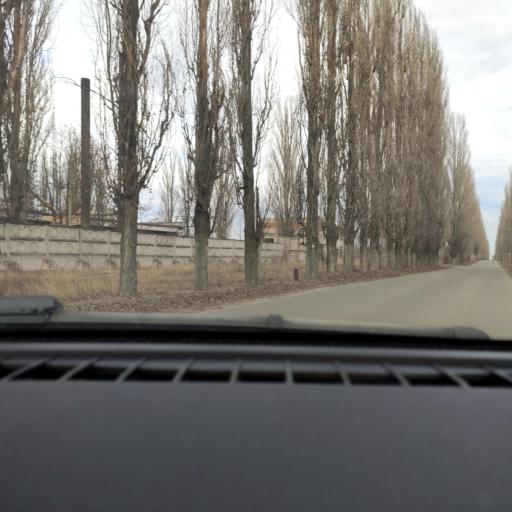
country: RU
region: Voronezj
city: Maslovka
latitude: 51.5989
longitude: 39.2207
